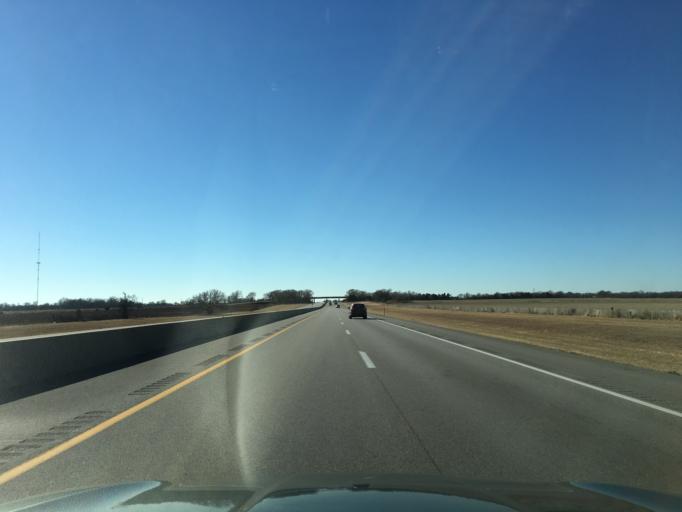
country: US
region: Kansas
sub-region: Sumner County
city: Belle Plaine
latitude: 37.3388
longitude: -97.3269
